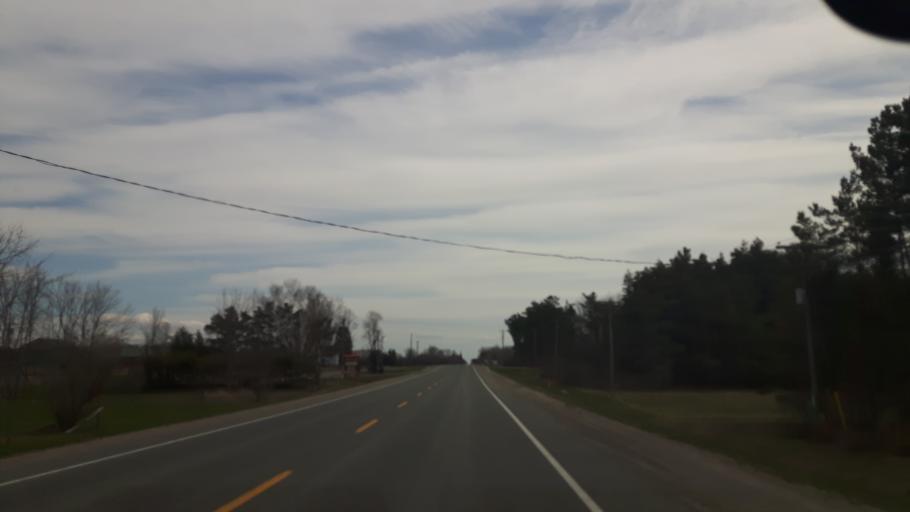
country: CA
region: Ontario
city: Goderich
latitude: 43.7095
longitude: -81.7057
